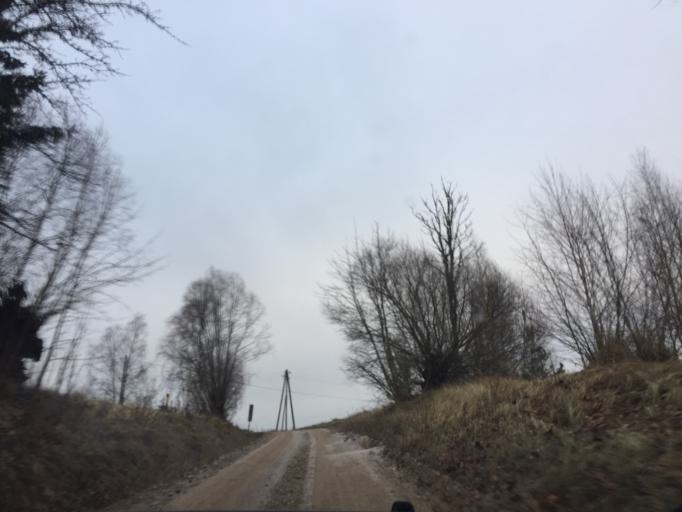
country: LV
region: Raunas
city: Rauna
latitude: 57.3048
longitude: 25.5863
